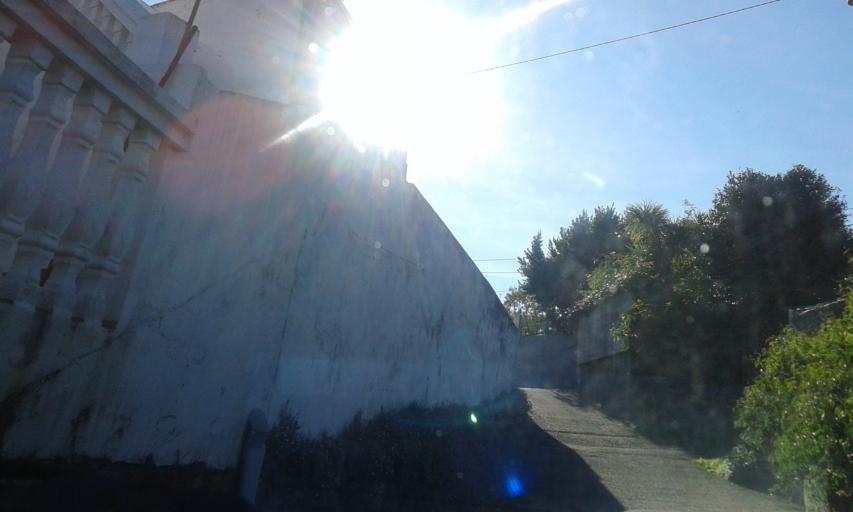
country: ES
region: Galicia
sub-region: Provincia de Pontevedra
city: Marin
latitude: 42.3720
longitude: -8.7366
